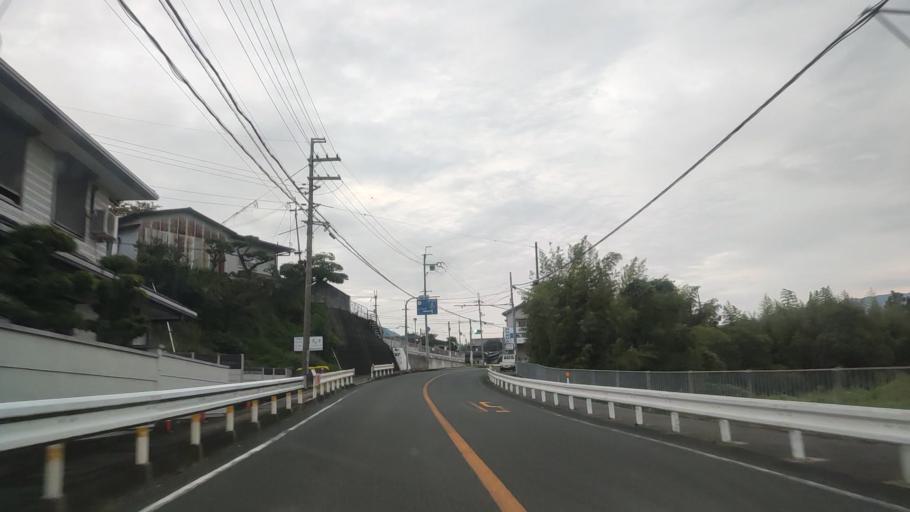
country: JP
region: Wakayama
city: Hashimoto
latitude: 34.3332
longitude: 135.6060
